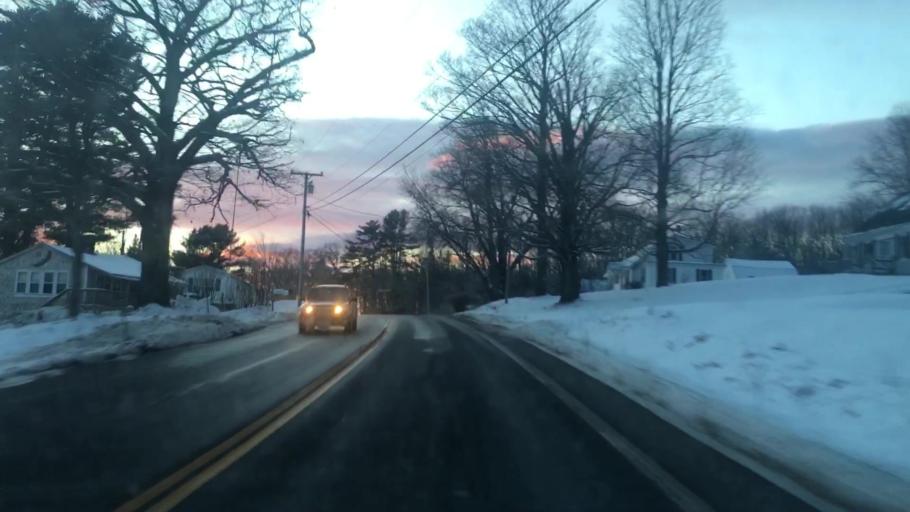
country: US
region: Maine
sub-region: Kennebec County
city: Pittston
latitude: 44.2225
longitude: -69.7347
